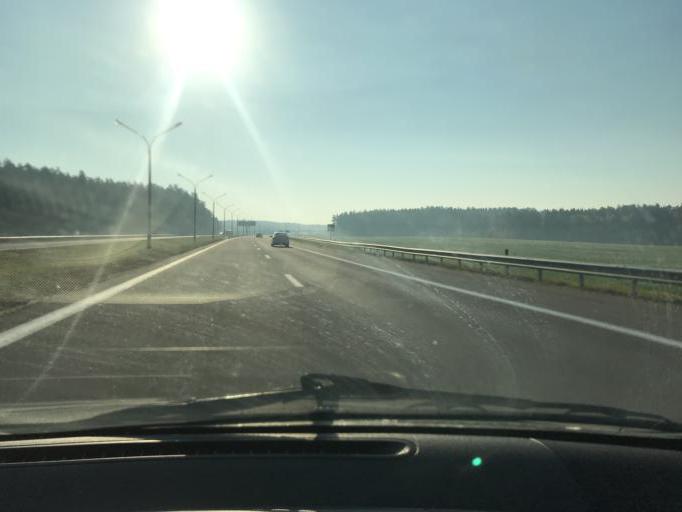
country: BY
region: Minsk
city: Slabada
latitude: 53.9566
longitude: 27.9696
